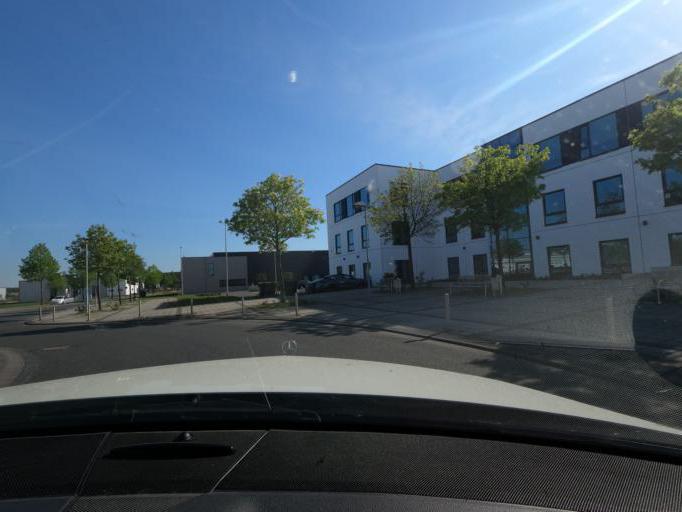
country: DE
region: North Rhine-Westphalia
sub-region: Regierungsbezirk Dusseldorf
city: Moers
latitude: 51.4725
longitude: 6.5947
